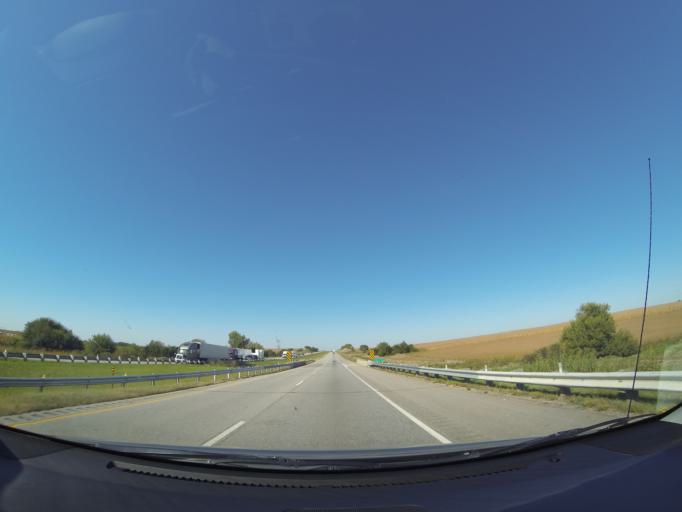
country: US
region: Nebraska
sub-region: Seward County
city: Seward
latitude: 40.8224
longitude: -97.1353
